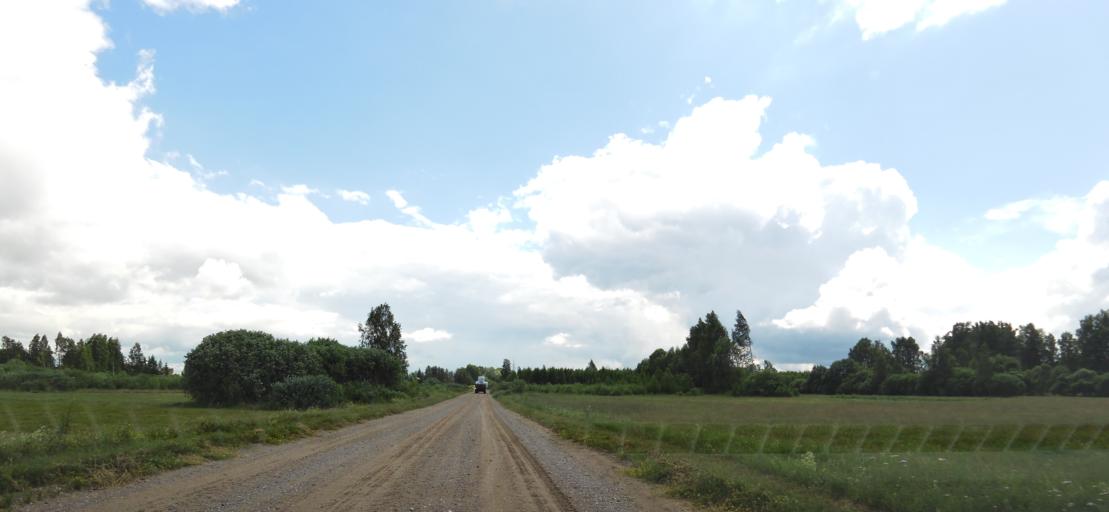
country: LT
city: Vabalninkas
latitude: 55.8842
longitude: 24.7728
